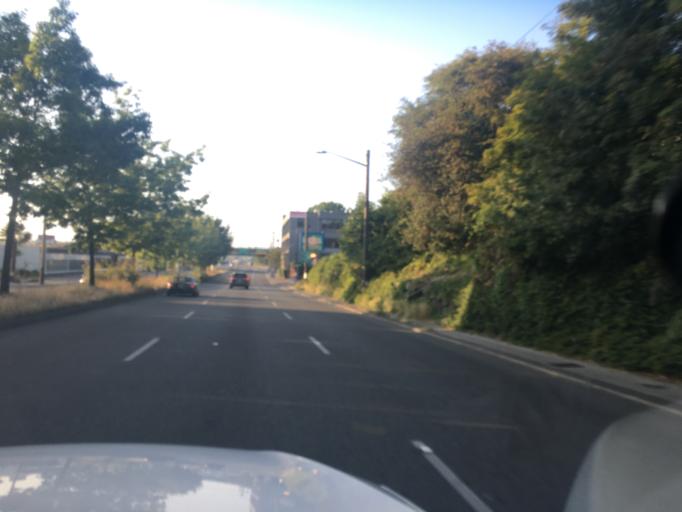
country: US
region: Washington
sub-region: King County
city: Seattle
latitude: 47.6513
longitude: -122.3762
